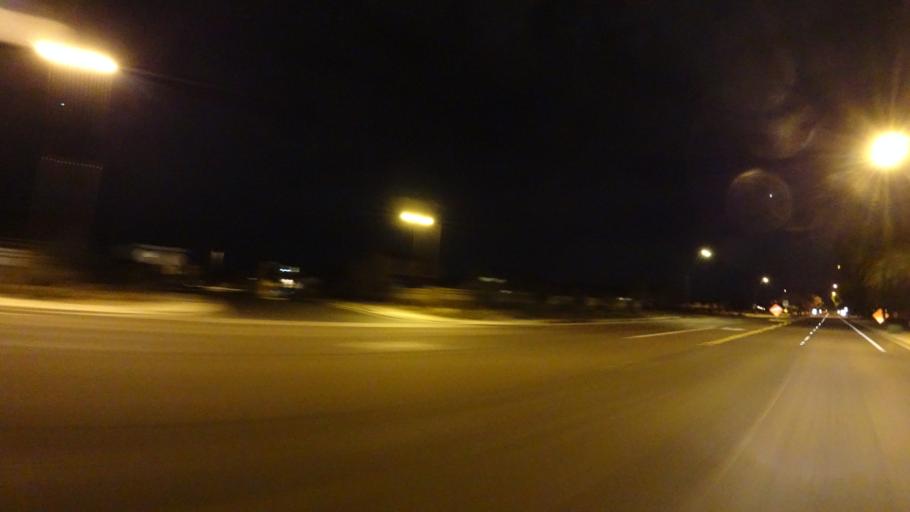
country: US
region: Arizona
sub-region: Maricopa County
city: Queen Creek
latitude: 33.2634
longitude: -111.6585
